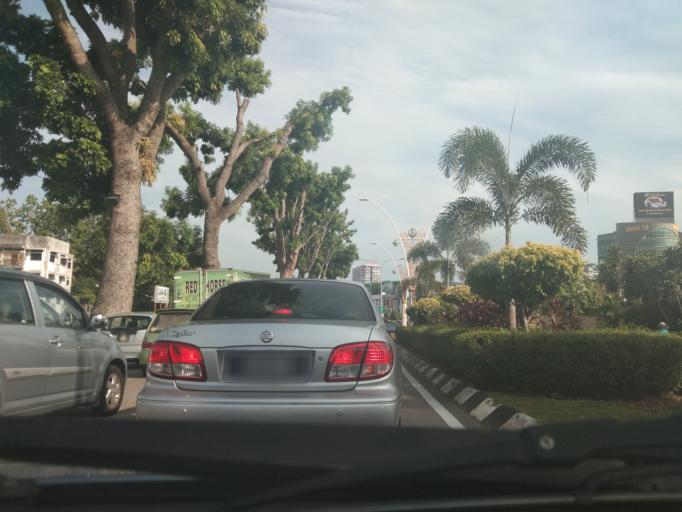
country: MY
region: Perak
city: Ipoh
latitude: 4.5911
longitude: 101.0911
